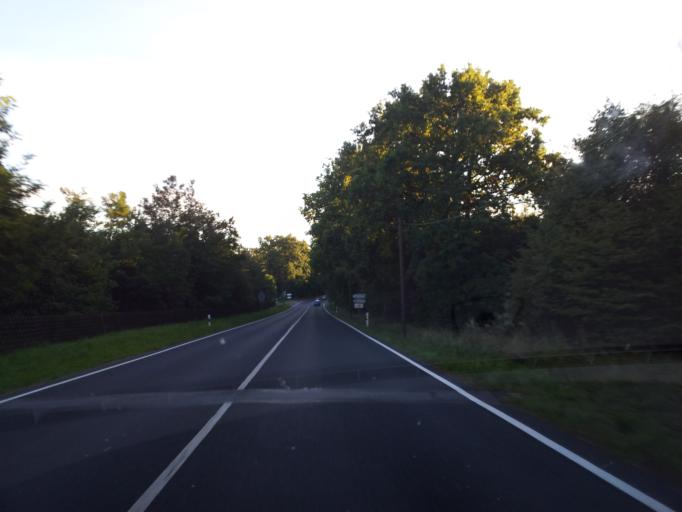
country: DE
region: Saxony
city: Ottendorf-Okrilla
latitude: 51.2083
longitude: 13.8387
